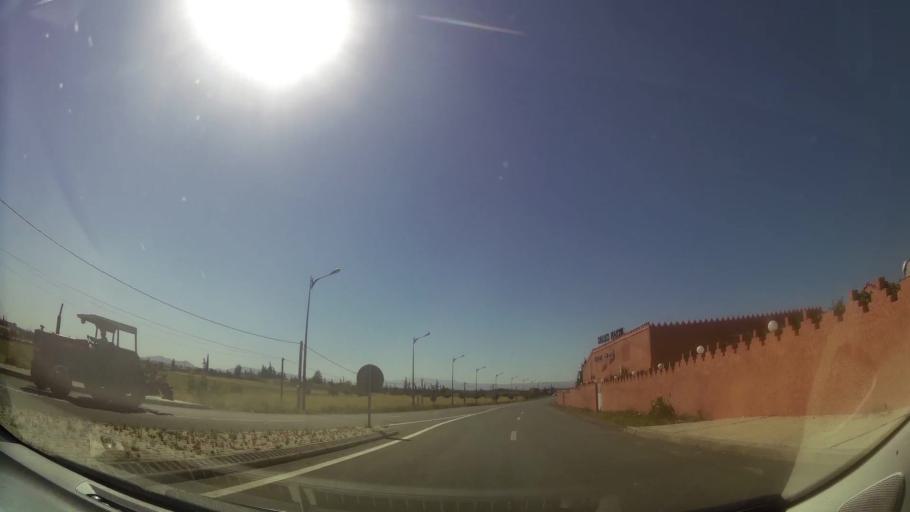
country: MA
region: Oriental
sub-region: Oujda-Angad
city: Oujda
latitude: 34.7322
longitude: -1.8737
